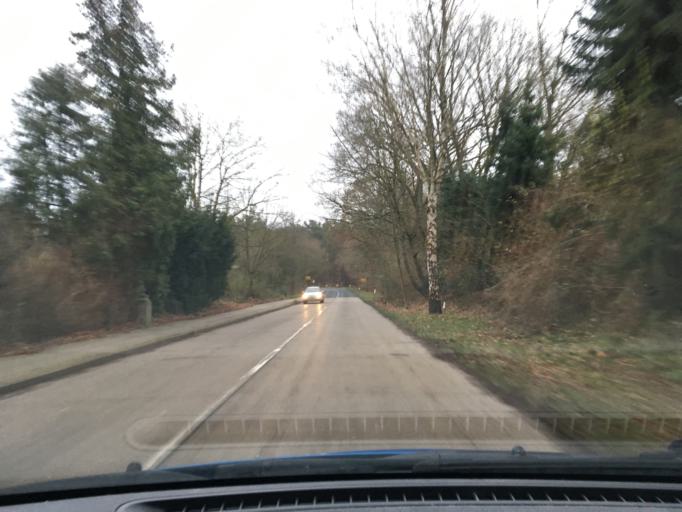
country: DE
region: Lower Saxony
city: Bleckede
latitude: 53.2802
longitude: 10.7579
